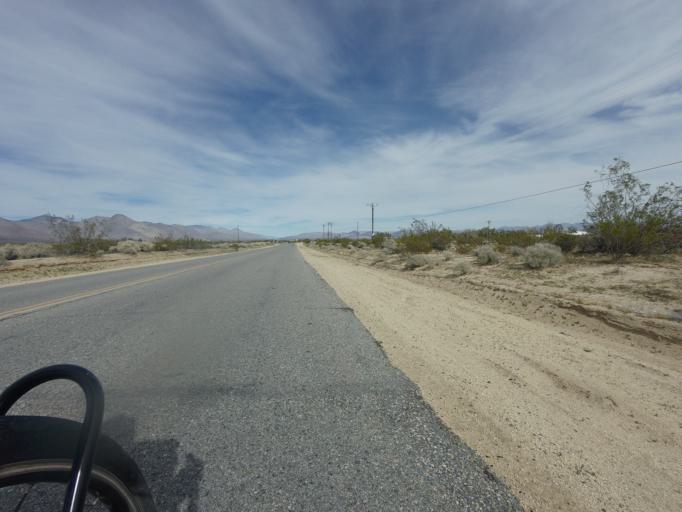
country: US
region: California
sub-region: Kern County
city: Inyokern
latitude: 35.7089
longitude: -117.8311
